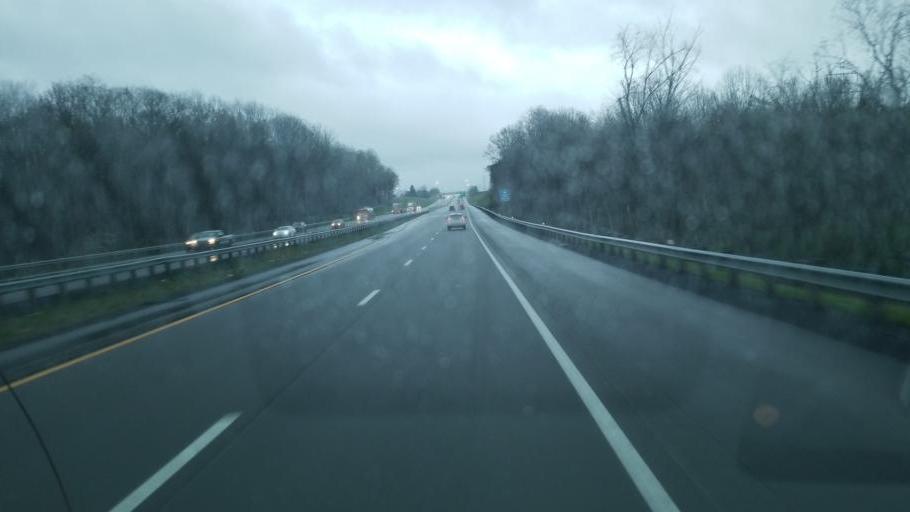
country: US
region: Ohio
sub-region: Summit County
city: Norton
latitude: 41.0400
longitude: -81.6812
